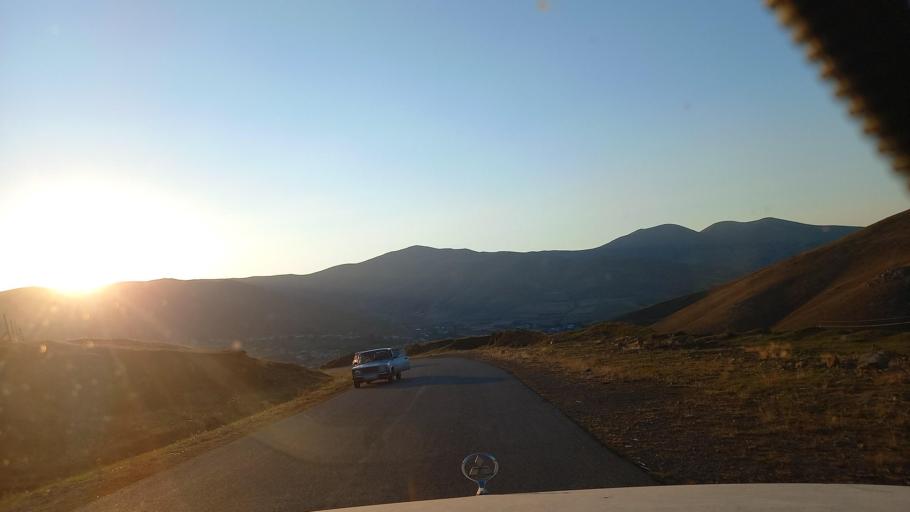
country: AZ
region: Gadabay Rayon
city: Ariqdam
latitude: 40.6832
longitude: 45.7771
